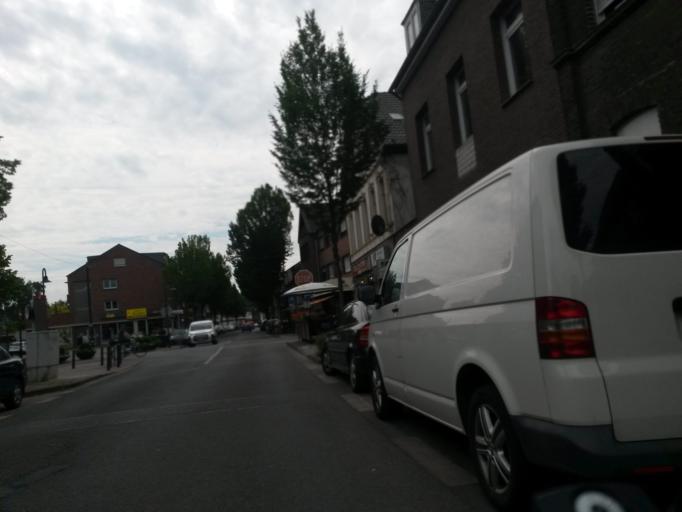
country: DE
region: North Rhine-Westphalia
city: Kempen
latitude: 51.3846
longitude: 6.4507
